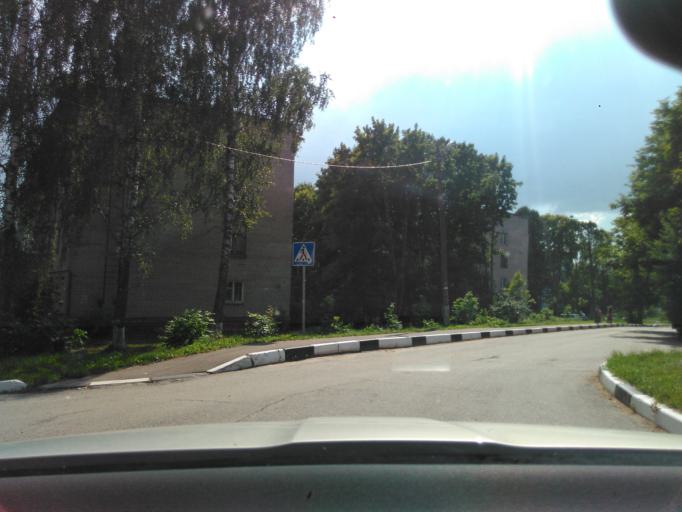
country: RU
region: Moskovskaya
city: Peshki
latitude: 56.1475
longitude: 37.0578
